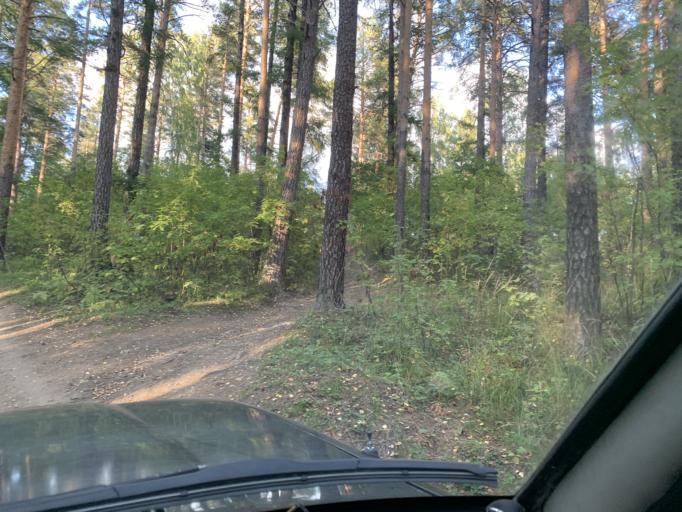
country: RU
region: Chelyabinsk
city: Vishnevogorsk
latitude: 55.9970
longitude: 60.5039
